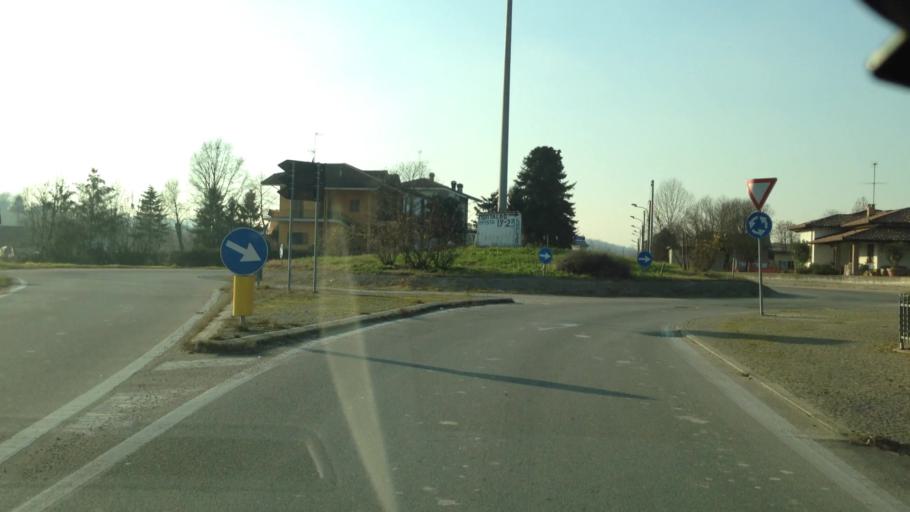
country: IT
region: Piedmont
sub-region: Provincia di Asti
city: Montaldo Scarampi
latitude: 44.8164
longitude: 8.2559
